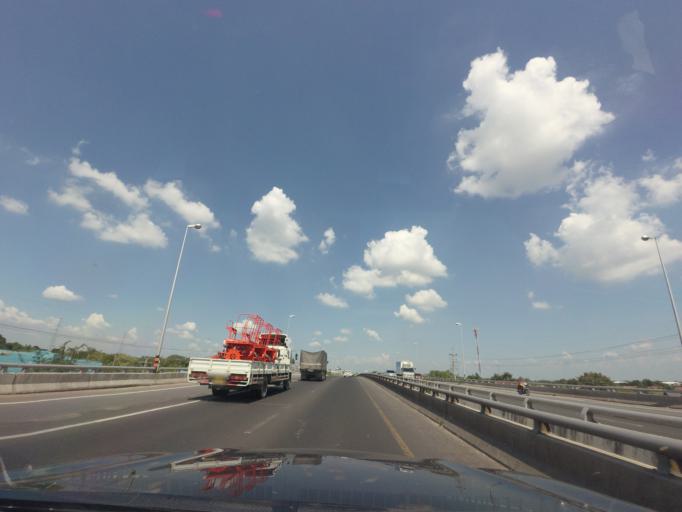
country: TH
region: Nakhon Ratchasima
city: Nakhon Ratchasima
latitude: 15.0577
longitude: 102.1640
